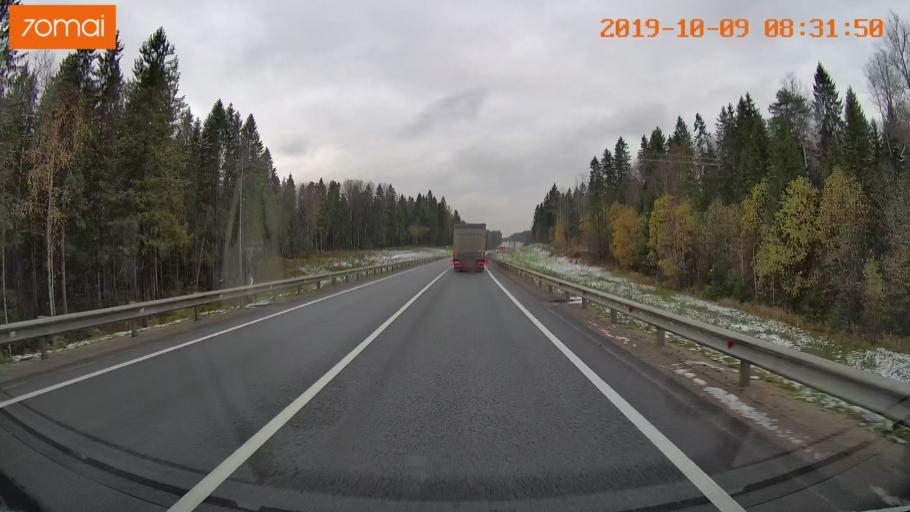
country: RU
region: Vologda
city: Gryazovets
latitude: 58.8590
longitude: 40.1995
